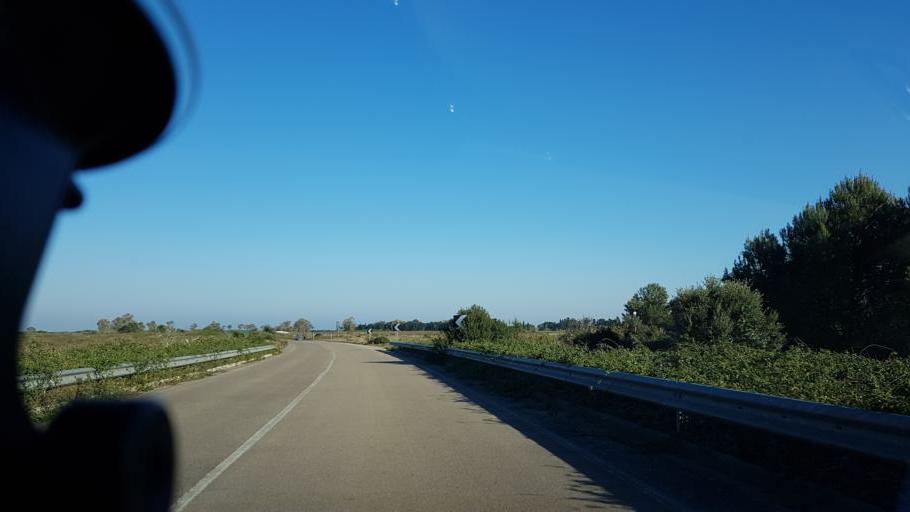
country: IT
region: Apulia
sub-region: Provincia di Lecce
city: Merine
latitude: 40.3945
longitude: 18.2562
